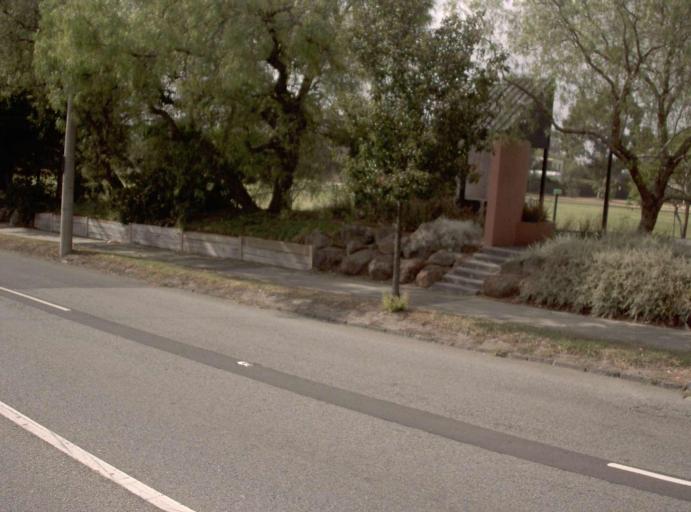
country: AU
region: Victoria
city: Glenferrie
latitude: -37.8443
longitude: 145.0357
